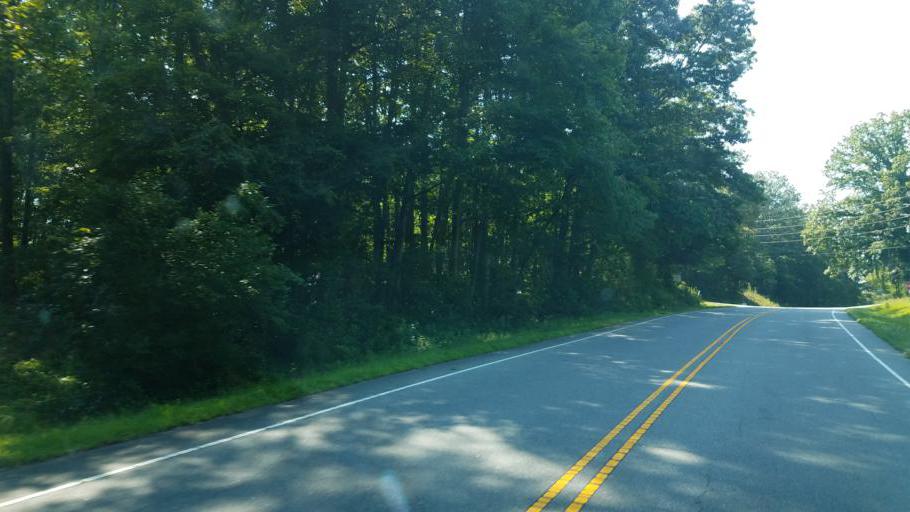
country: US
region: North Carolina
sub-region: Burke County
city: Glen Alpine
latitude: 35.8112
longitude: -81.7886
